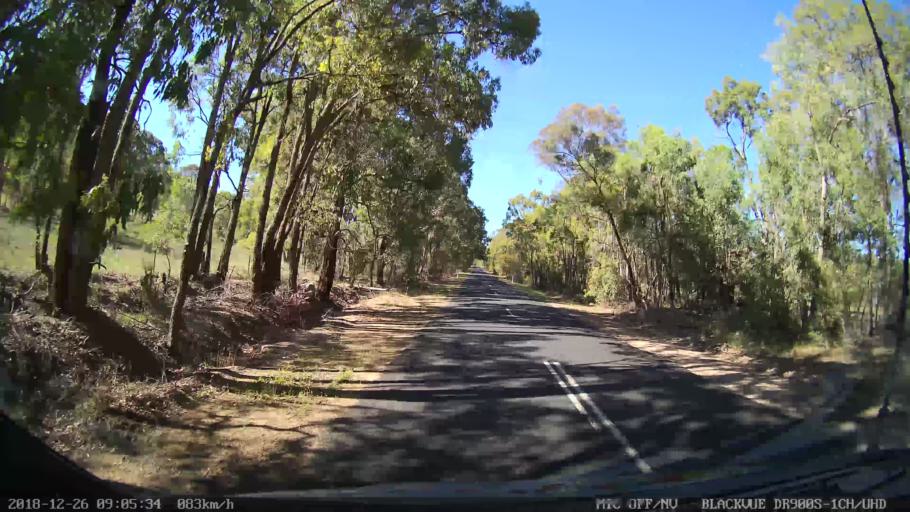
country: AU
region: New South Wales
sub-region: Mid-Western Regional
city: Kandos
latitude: -32.6841
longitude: 150.0067
